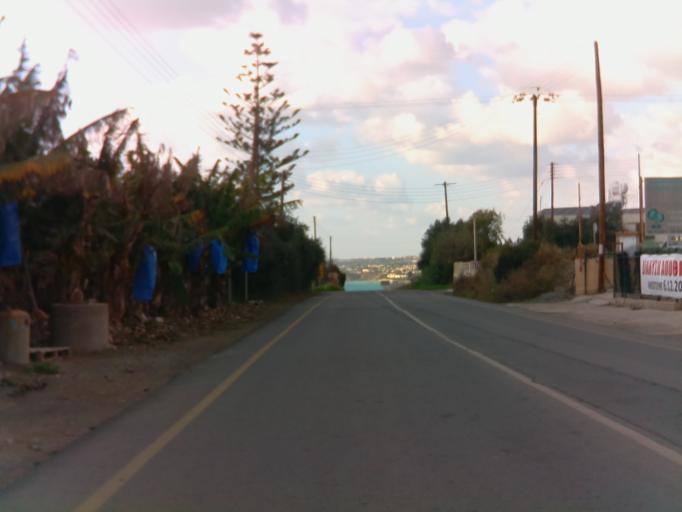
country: CY
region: Pafos
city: Kissonerga
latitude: 34.8276
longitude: 32.3972
